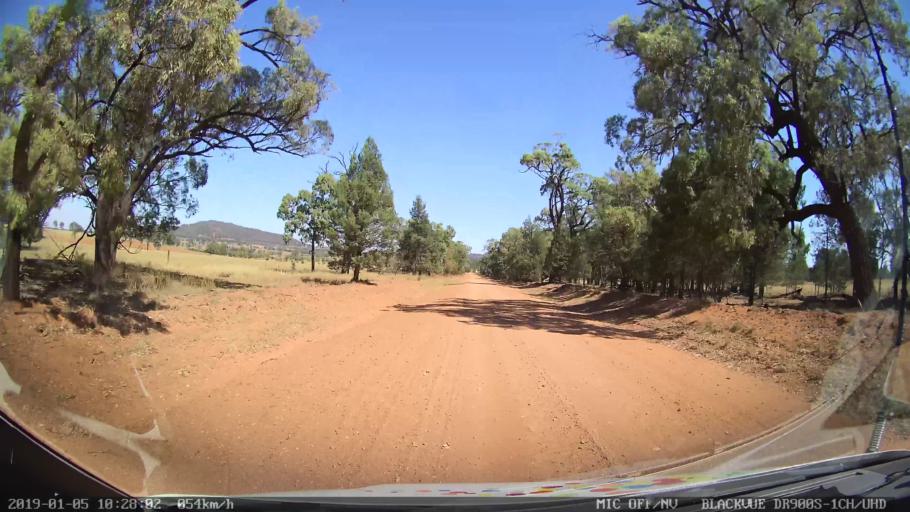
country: AU
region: New South Wales
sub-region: Gilgandra
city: Gilgandra
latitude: -31.5476
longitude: 148.9416
